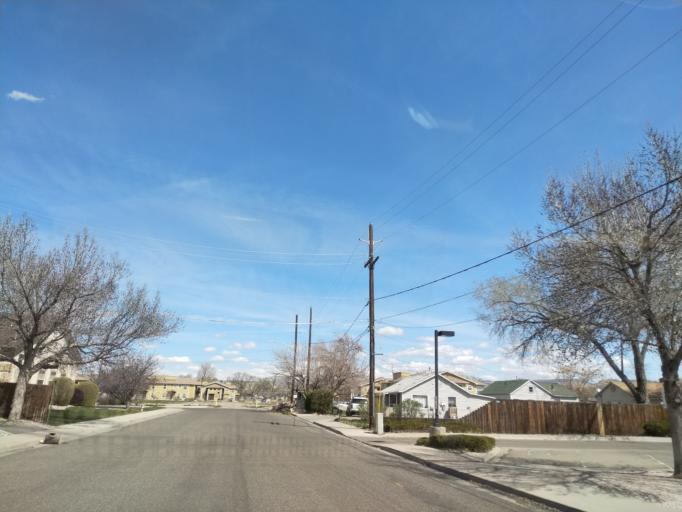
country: US
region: Colorado
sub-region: Mesa County
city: Grand Junction
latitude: 39.0785
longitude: -108.5320
